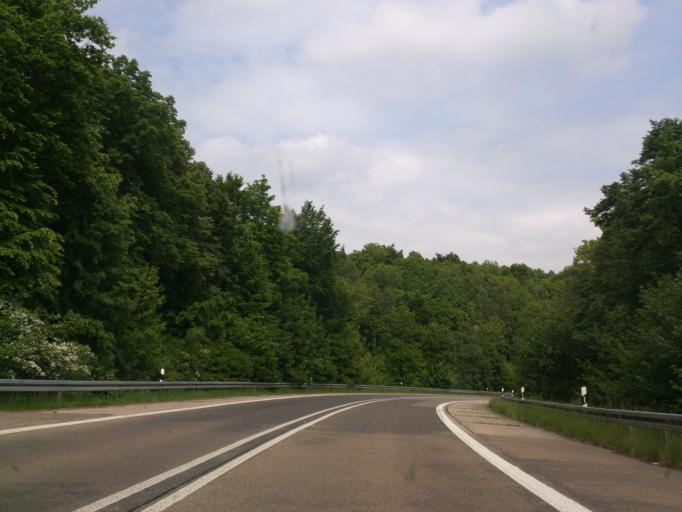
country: DE
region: Hesse
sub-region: Regierungsbezirk Kassel
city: Baunatal
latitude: 51.2791
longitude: 9.3996
